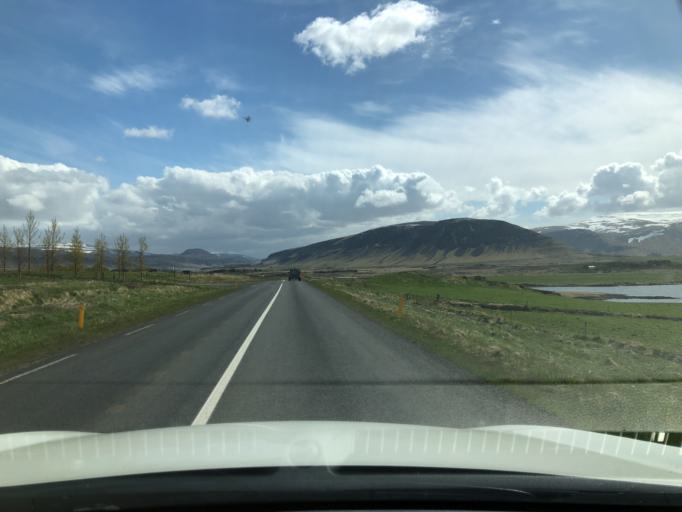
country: IS
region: Capital Region
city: Mosfellsbaer
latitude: 64.3487
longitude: -21.6263
